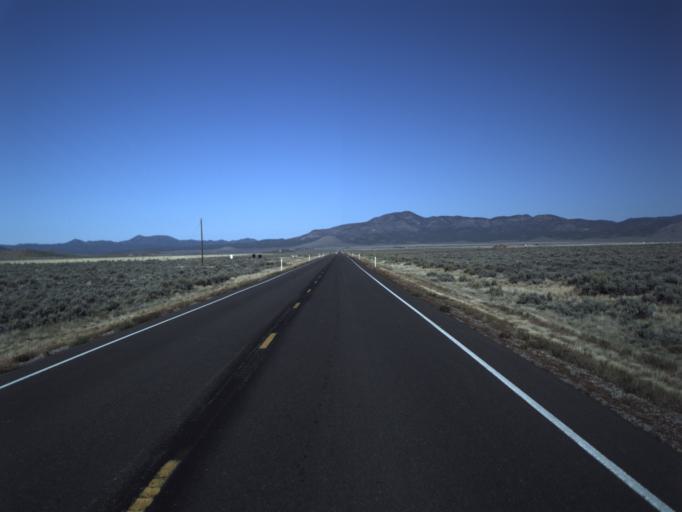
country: US
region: Utah
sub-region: Washington County
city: Enterprise
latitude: 37.7665
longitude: -113.8176
